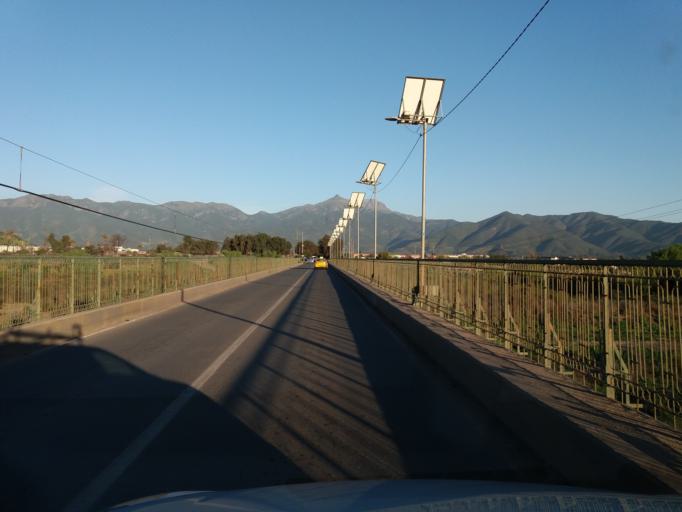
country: CL
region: Valparaiso
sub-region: Provincia de Quillota
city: Quillota
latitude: -32.8768
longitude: -71.2662
